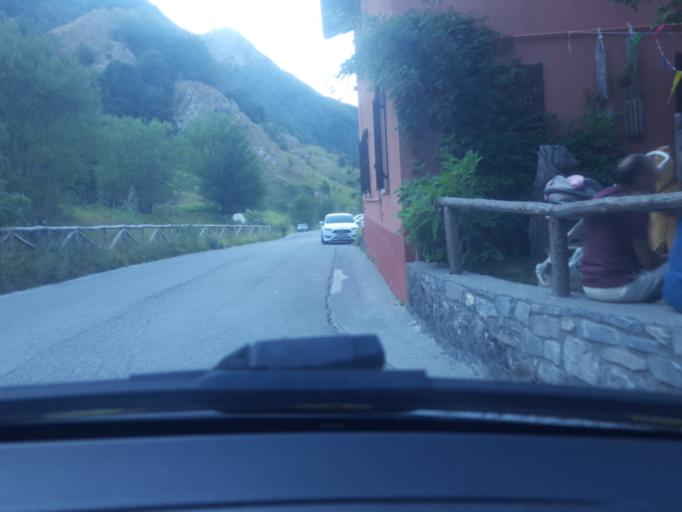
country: IT
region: Tuscany
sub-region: Provincia di Lucca
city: Minucciano
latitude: 44.1340
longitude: 10.1975
